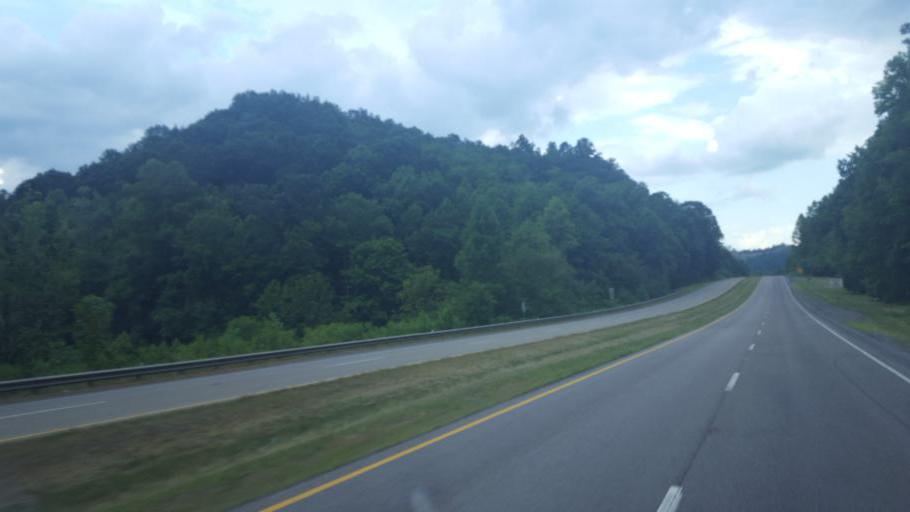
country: US
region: Virginia
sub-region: Wise County
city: Pound
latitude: 37.1258
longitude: -82.6212
